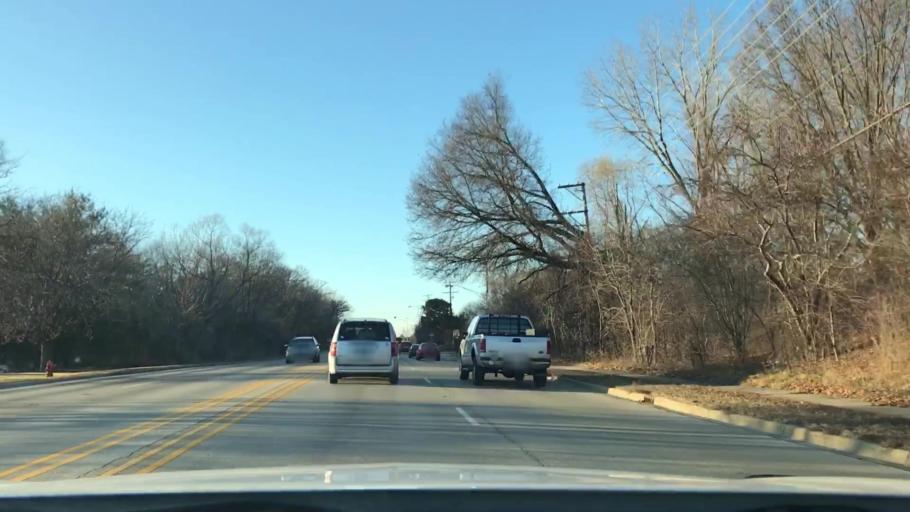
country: US
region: Illinois
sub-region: Kane County
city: Sleepy Hollow
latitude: 42.0624
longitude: -88.3300
